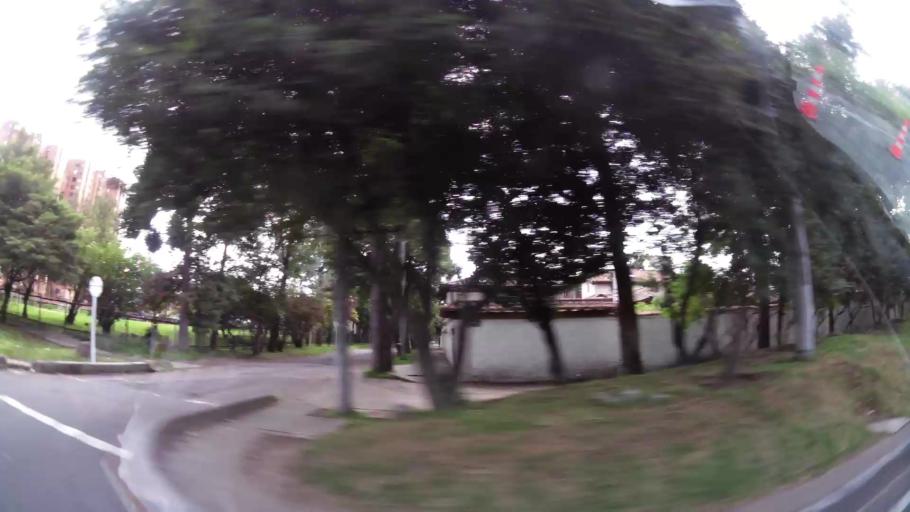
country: CO
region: Bogota D.C.
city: Barrio San Luis
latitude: 4.7167
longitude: -74.0758
